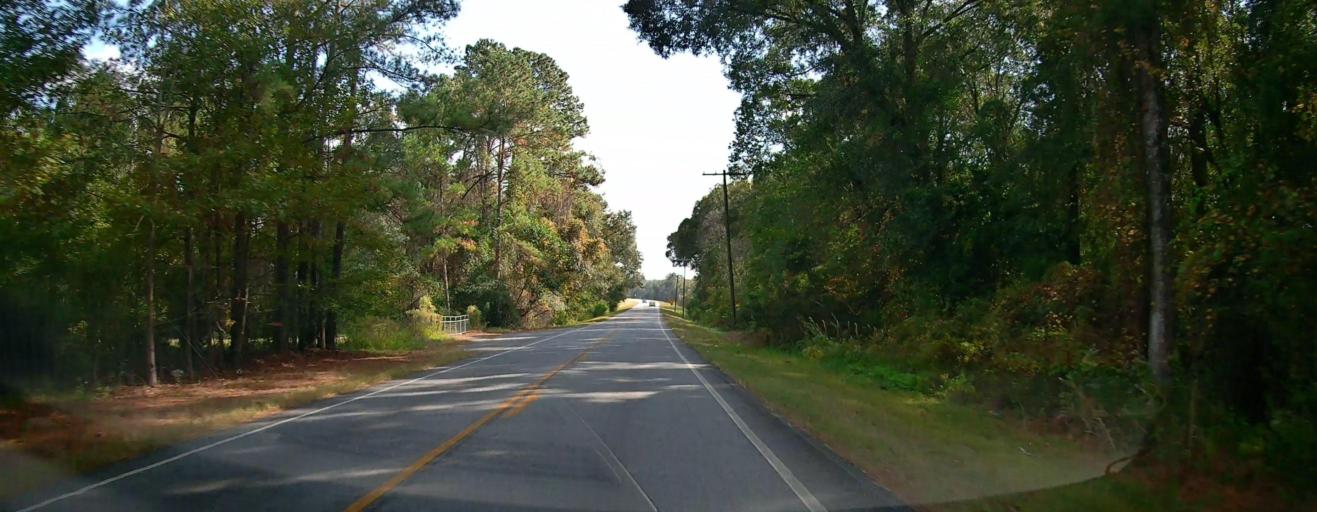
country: US
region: Georgia
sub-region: Thomas County
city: Thomasville
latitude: 30.9202
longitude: -84.0127
